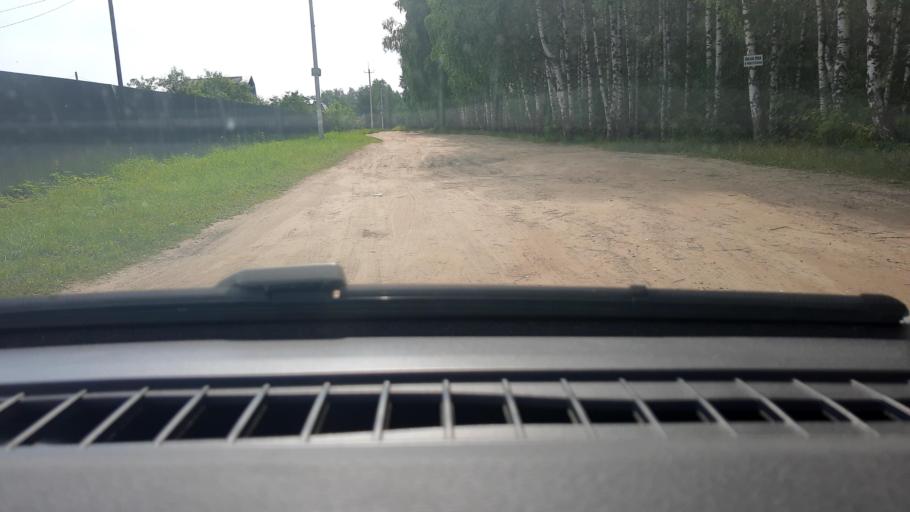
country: RU
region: Nizjnij Novgorod
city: Neklyudovo
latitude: 56.4286
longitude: 43.9981
